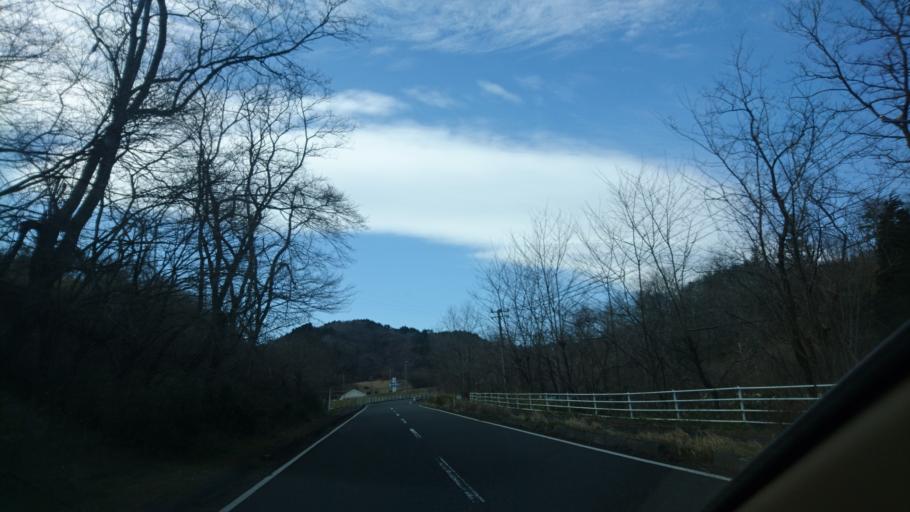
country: JP
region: Miyagi
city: Furukawa
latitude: 38.8069
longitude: 140.9032
